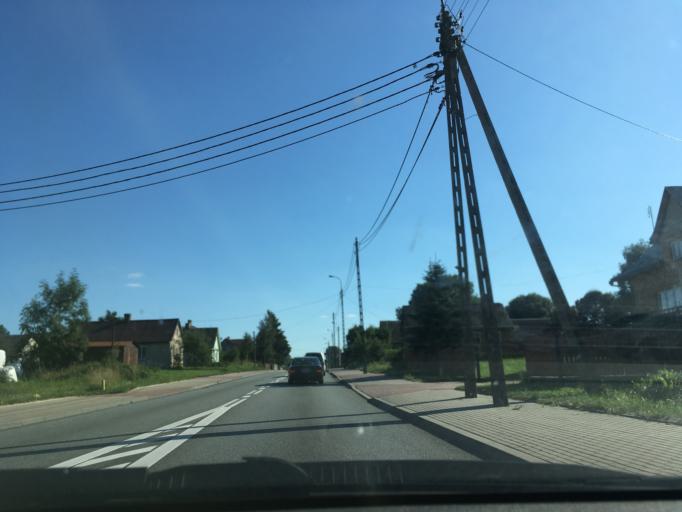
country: PL
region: Podlasie
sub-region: Powiat sokolski
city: Suchowola
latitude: 53.5041
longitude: 23.0981
